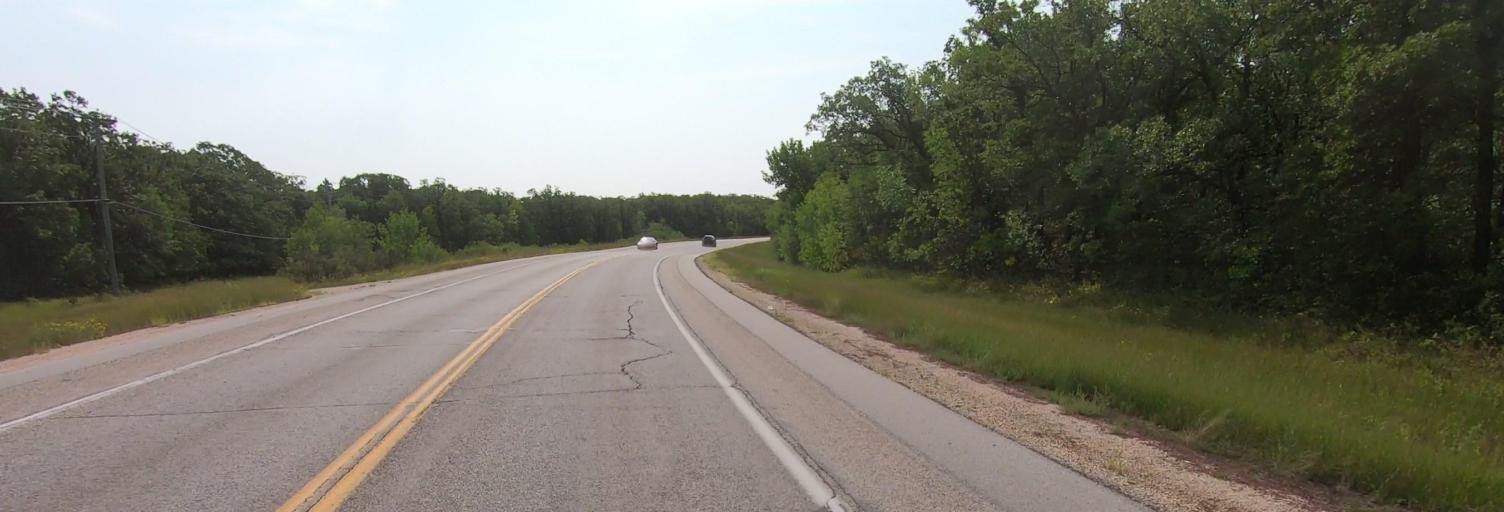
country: CA
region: Manitoba
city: Niverville
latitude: 49.7276
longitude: -97.0928
